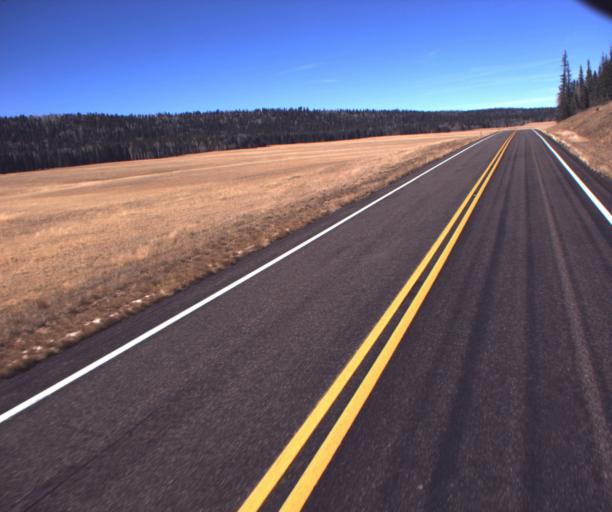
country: US
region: Arizona
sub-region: Coconino County
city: Grand Canyon
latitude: 36.3742
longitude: -112.1244
